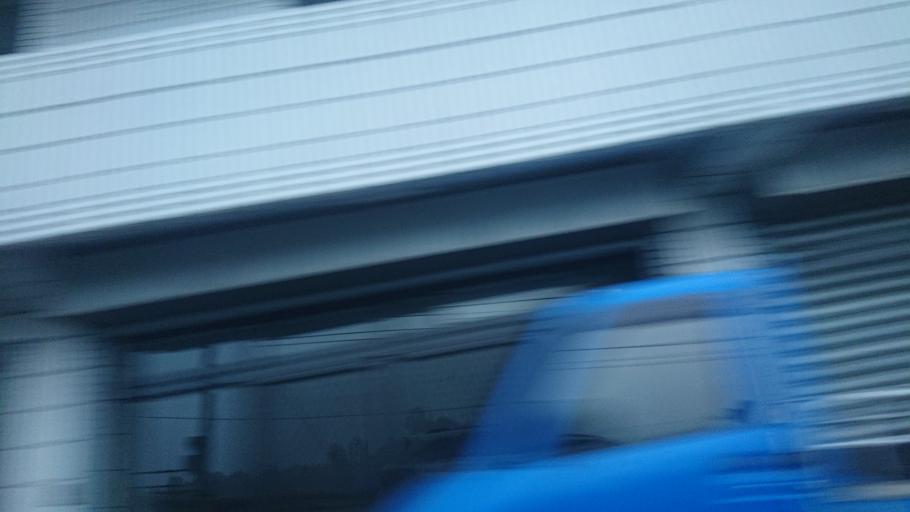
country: TW
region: Taiwan
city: Lugu
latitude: 23.5220
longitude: 120.7054
